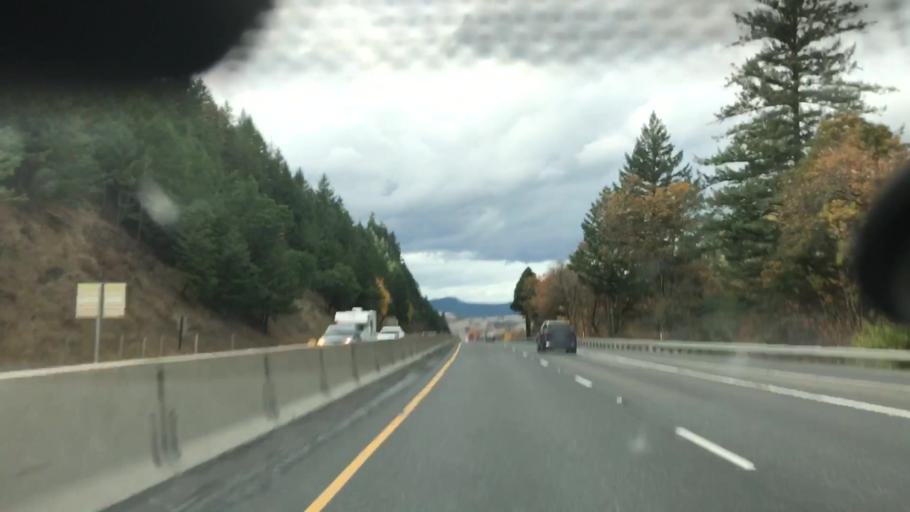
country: US
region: Oregon
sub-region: Douglas County
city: Sutherlin
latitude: 43.4387
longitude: -123.3148
